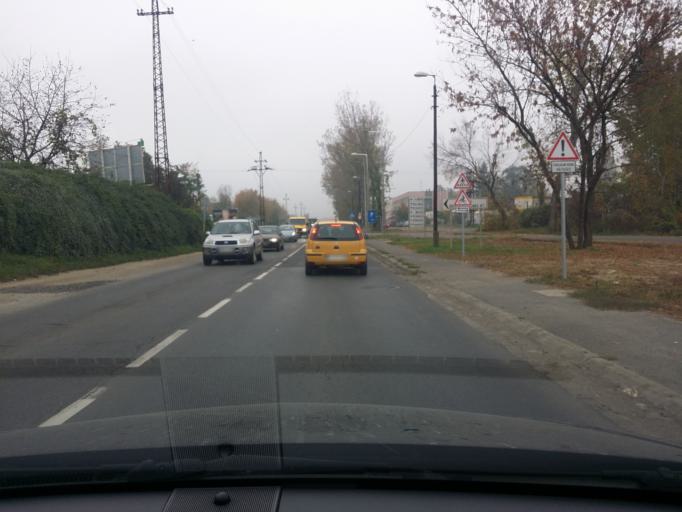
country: HU
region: Szabolcs-Szatmar-Bereg
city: Nyiregyhaza
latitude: 47.9651
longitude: 21.6987
